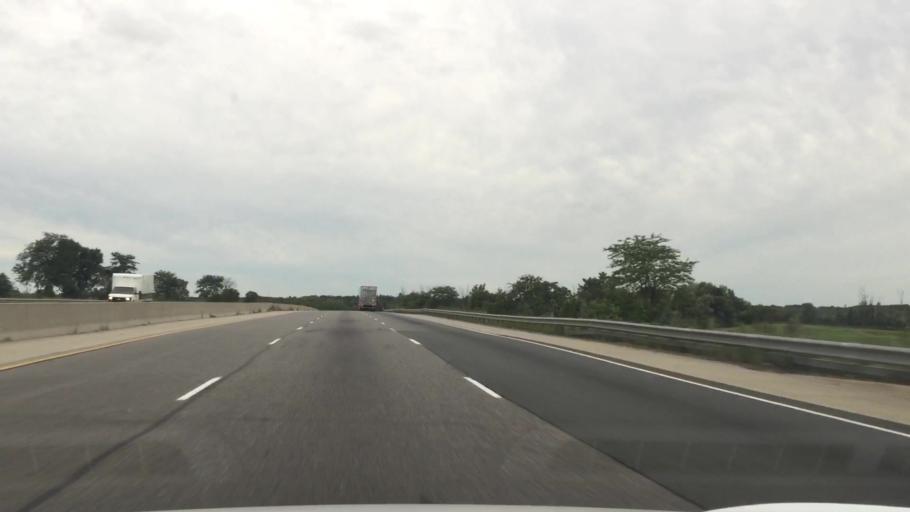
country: CA
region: Ontario
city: Kitchener
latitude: 43.2786
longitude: -80.5230
